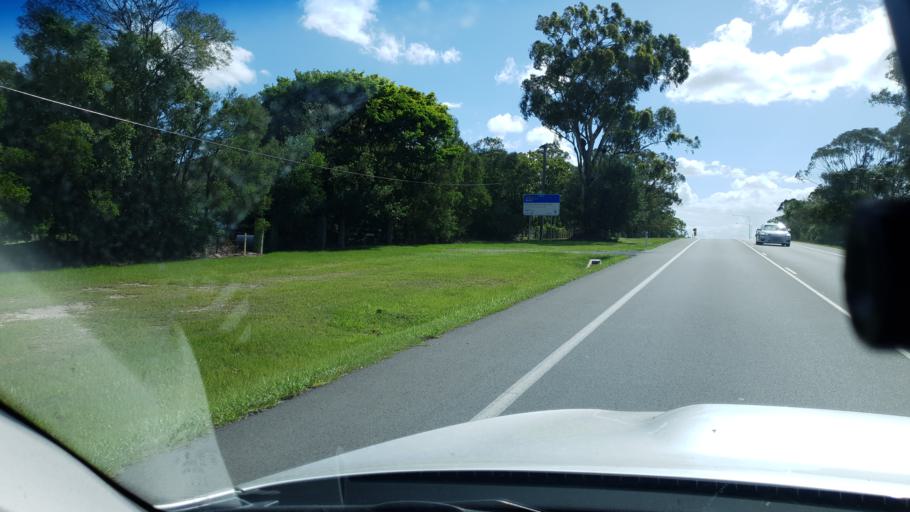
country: AU
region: Queensland
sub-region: Logan
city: Woodridge
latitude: -27.6505
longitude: 153.0820
